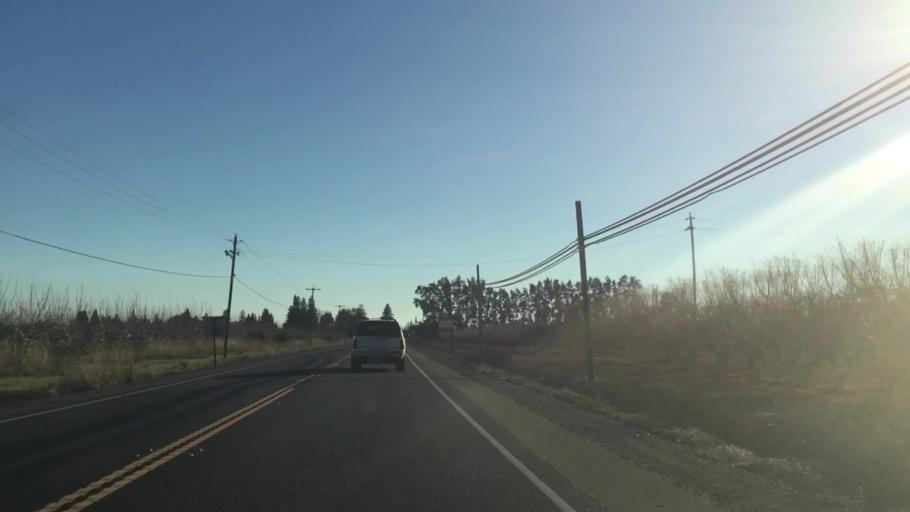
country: US
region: California
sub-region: Yuba County
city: Marysville
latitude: 39.1965
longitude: -121.5950
